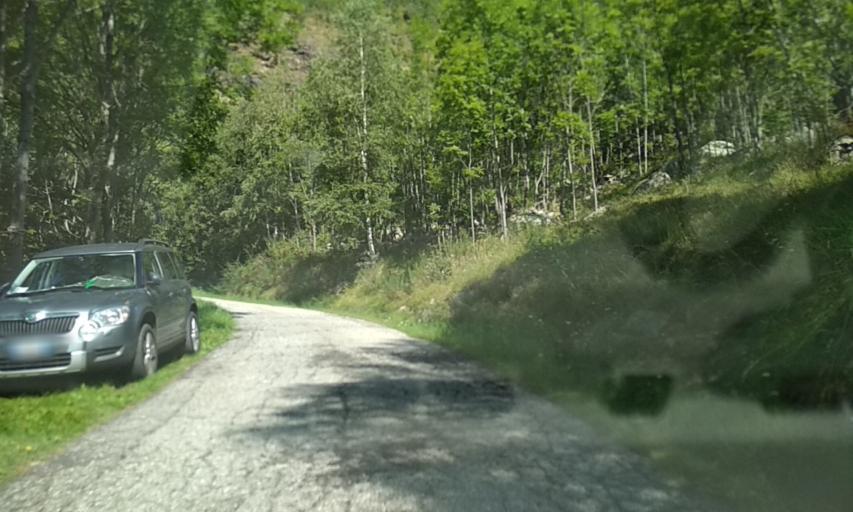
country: IT
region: Piedmont
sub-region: Provincia di Torino
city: Noasca
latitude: 45.4570
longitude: 7.3046
